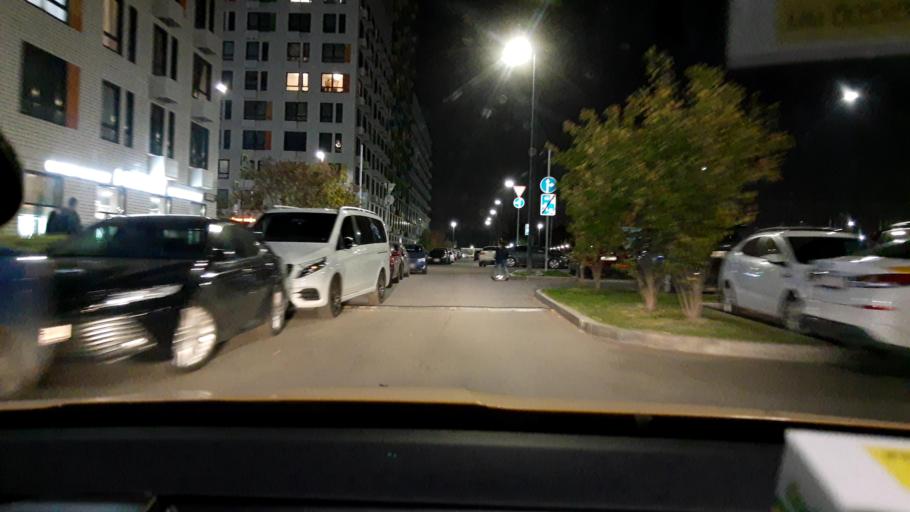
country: RU
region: Moskovskaya
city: Kommunarka
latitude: 55.5434
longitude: 37.4877
